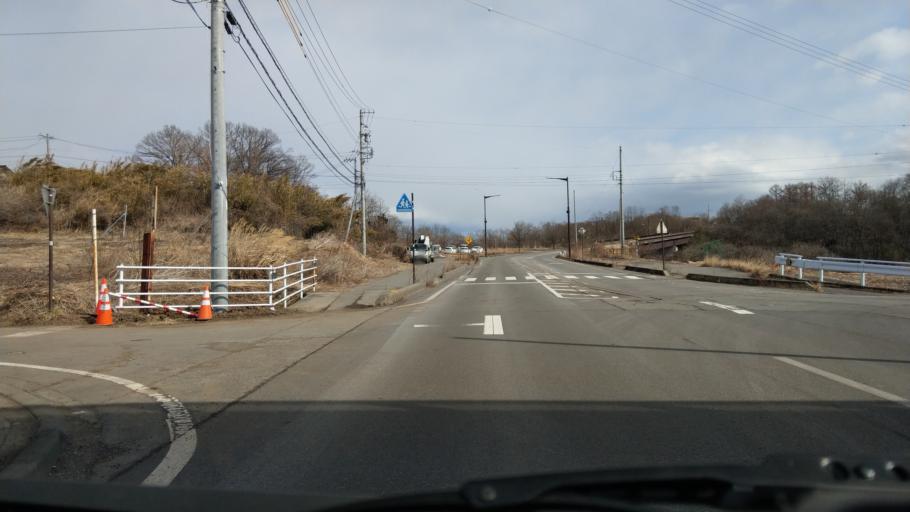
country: JP
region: Nagano
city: Komoro
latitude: 36.2826
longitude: 138.4031
